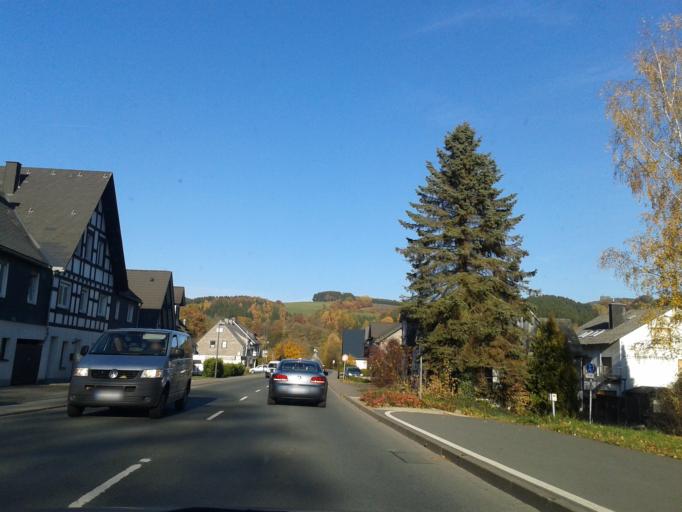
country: DE
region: North Rhine-Westphalia
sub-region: Regierungsbezirk Arnsberg
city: Olsberg
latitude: 51.3048
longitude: 8.4998
